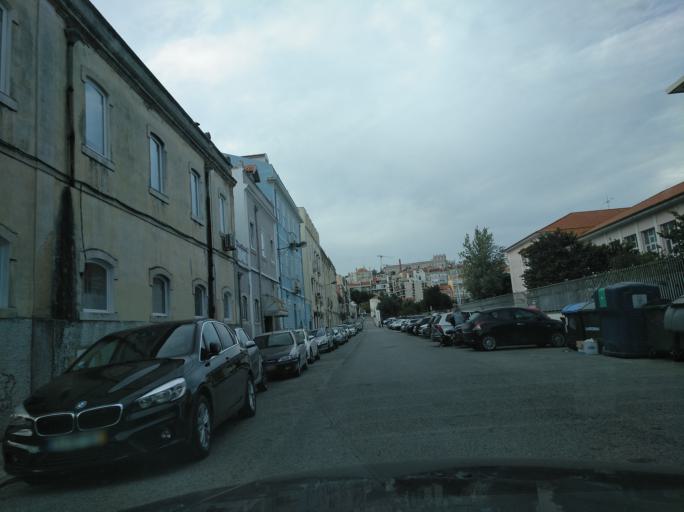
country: PT
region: Setubal
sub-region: Almada
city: Caparica
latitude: 38.6995
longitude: -9.1958
